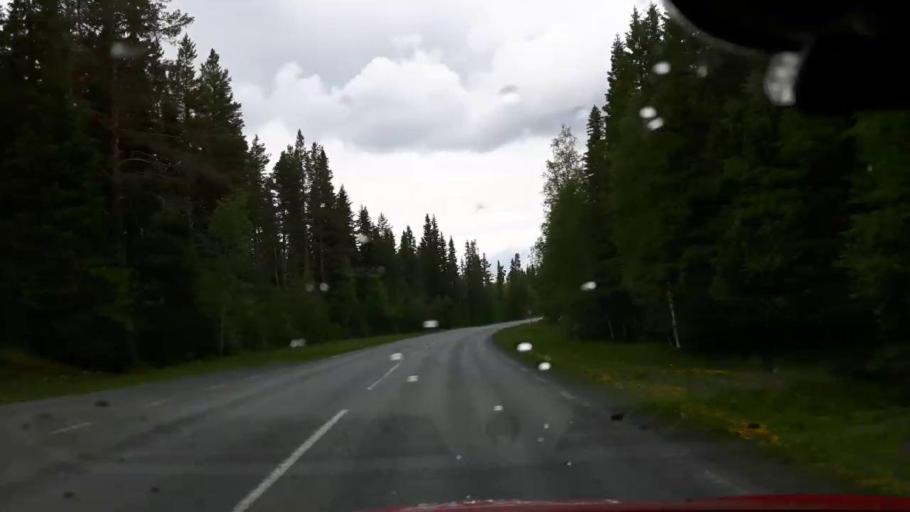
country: SE
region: Jaemtland
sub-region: Krokoms Kommun
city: Krokom
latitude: 63.4113
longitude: 14.2400
